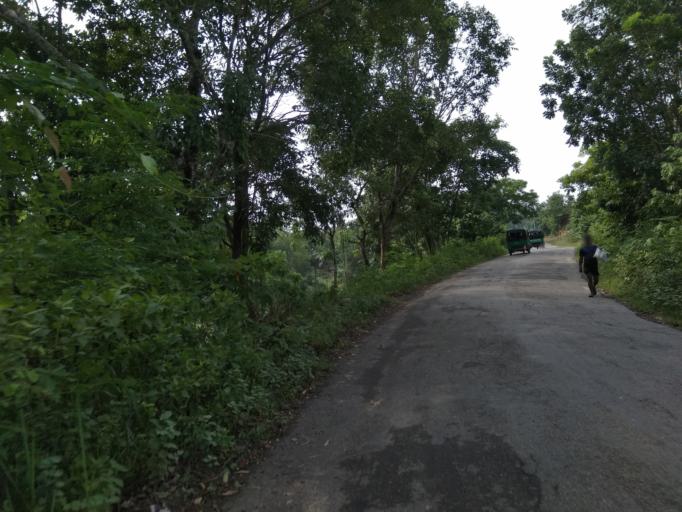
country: BD
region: Chittagong
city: Khagrachhari
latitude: 22.9961
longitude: 92.0124
